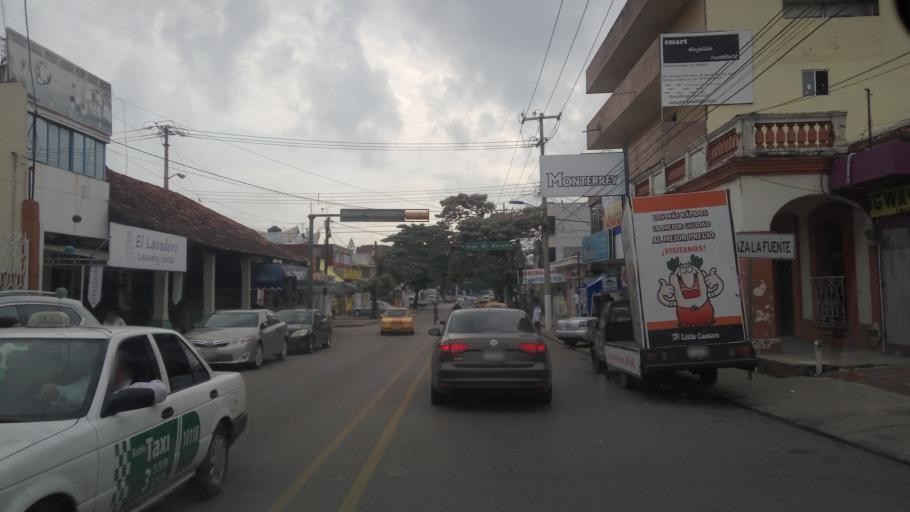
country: MX
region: Tabasco
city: Villahermosa
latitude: 17.9844
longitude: -92.9480
